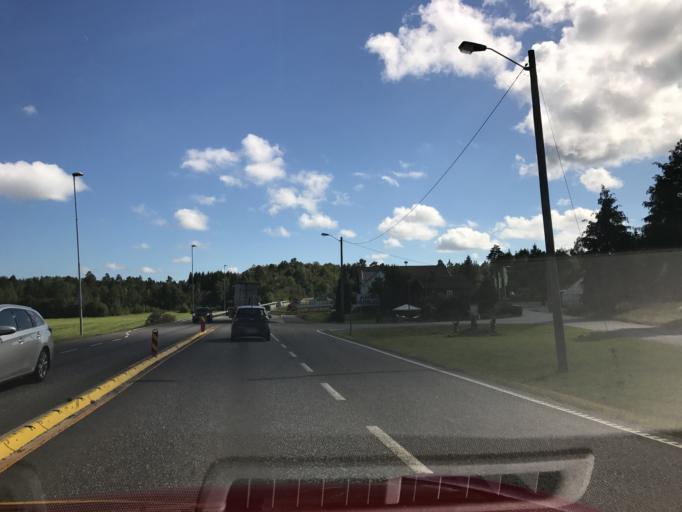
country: NO
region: Telemark
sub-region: Bamble
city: Langesund
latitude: 59.0300
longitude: 9.6791
